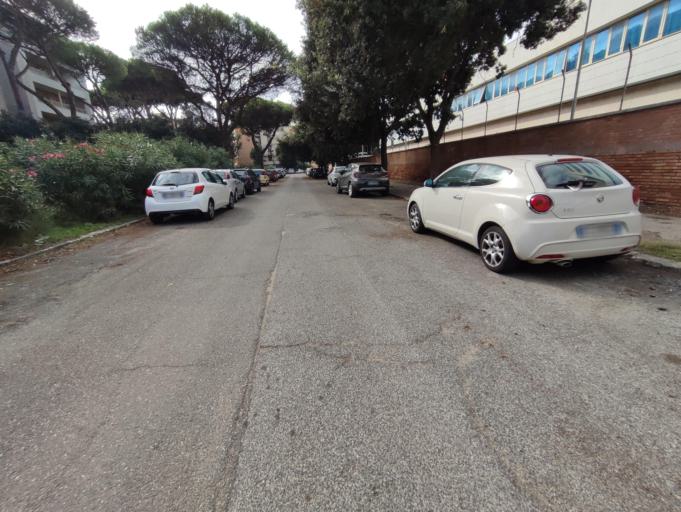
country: IT
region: Latium
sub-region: Citta metropolitana di Roma Capitale
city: Lido di Ostia
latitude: 41.7323
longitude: 12.2945
